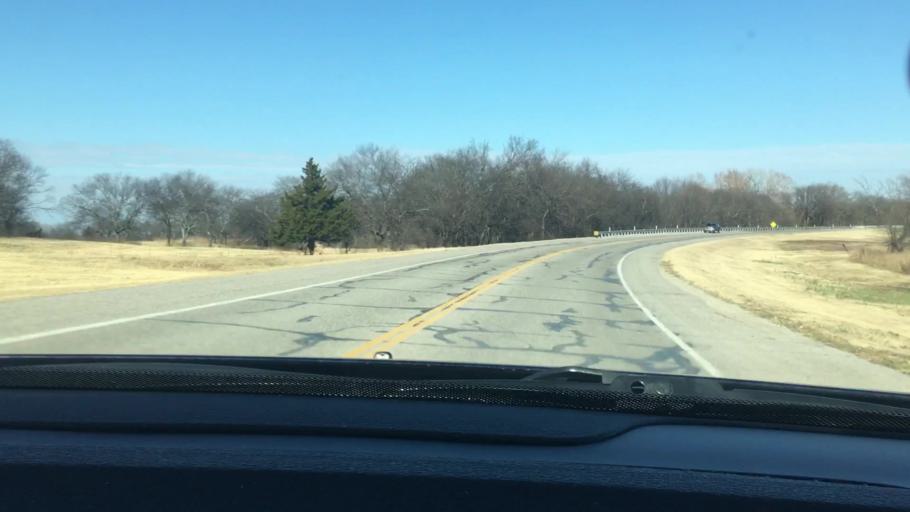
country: US
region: Oklahoma
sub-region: Murray County
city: Davis
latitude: 34.5106
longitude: -97.1224
